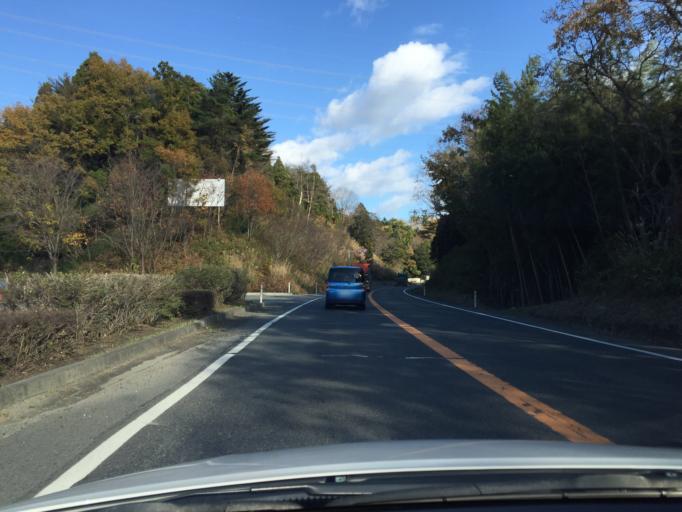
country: JP
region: Fukushima
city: Namie
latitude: 37.3145
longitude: 141.0007
